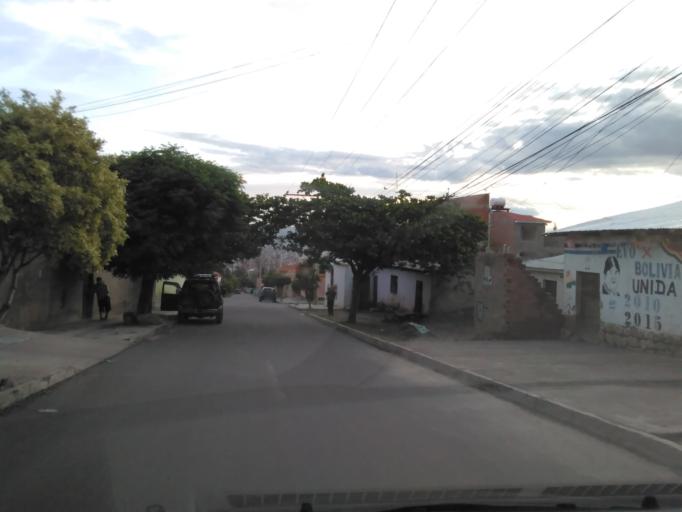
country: BO
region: Cochabamba
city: Cochabamba
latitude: -17.3593
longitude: -66.1613
